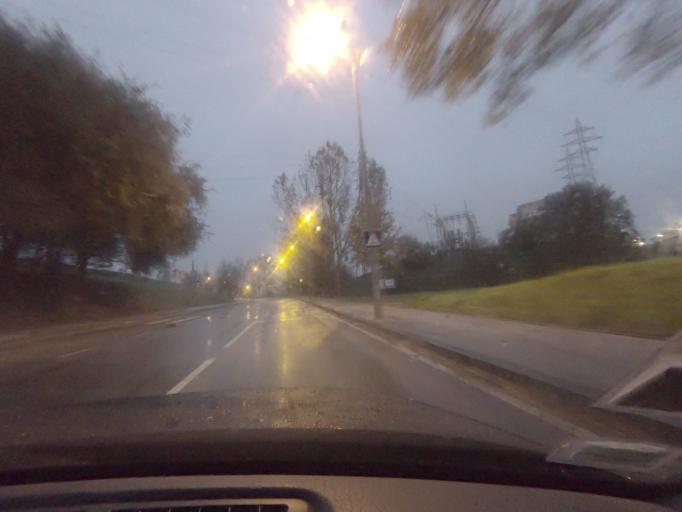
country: PT
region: Porto
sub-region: Matosinhos
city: Matosinhos
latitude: 41.1886
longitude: -8.6778
